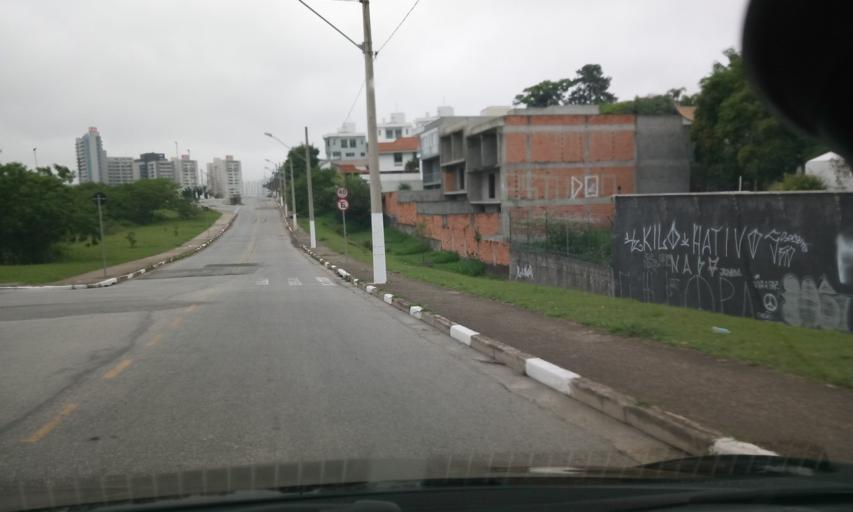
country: BR
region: Sao Paulo
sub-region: Sao Bernardo Do Campo
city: Sao Bernardo do Campo
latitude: -23.6792
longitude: -46.5633
